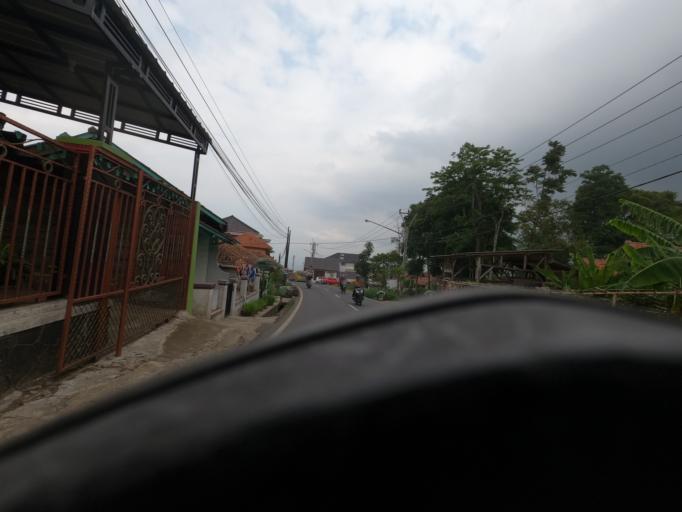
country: ID
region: West Java
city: Cimahi
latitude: -6.8189
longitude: 107.5382
